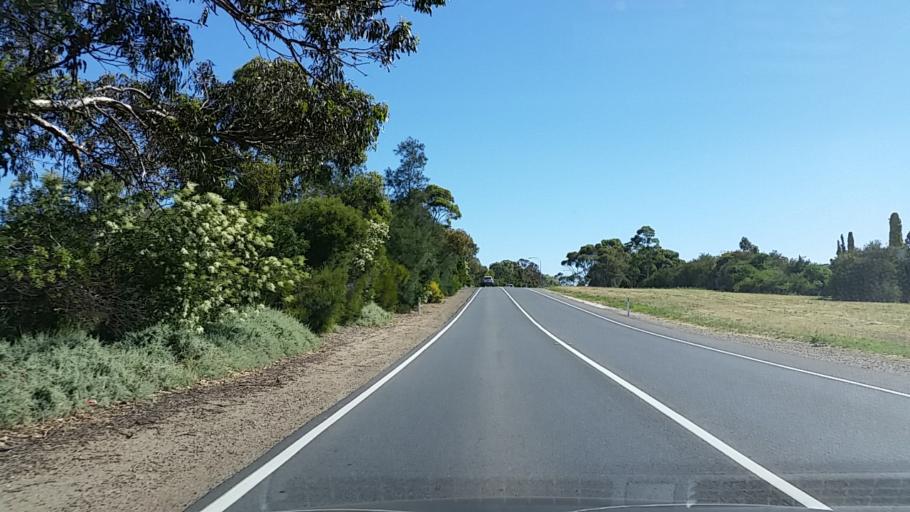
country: AU
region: South Australia
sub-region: Tea Tree Gully
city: Golden Grove
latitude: -34.8008
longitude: 138.7057
